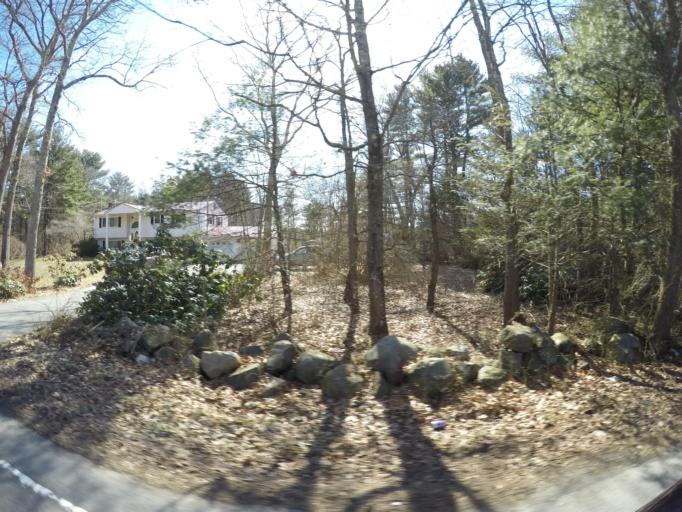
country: US
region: Massachusetts
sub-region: Bristol County
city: Easton
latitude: 42.0637
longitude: -71.1331
